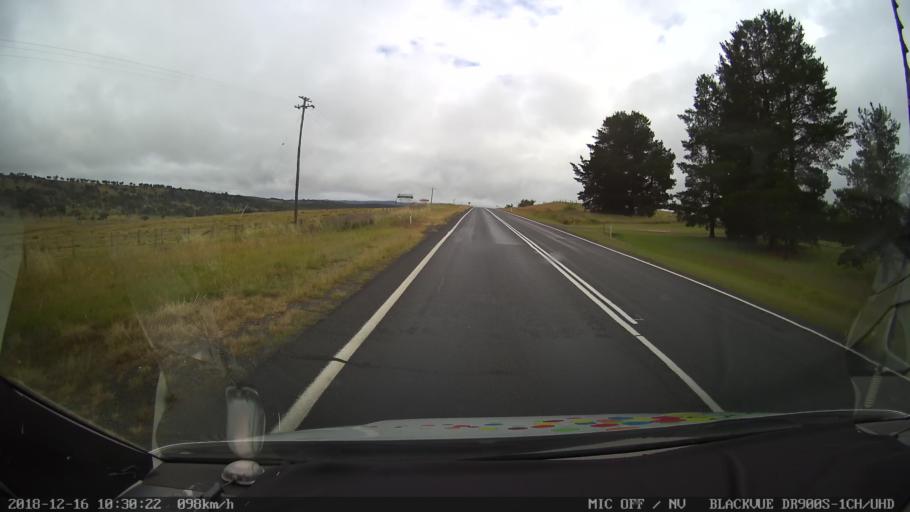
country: AU
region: New South Wales
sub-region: Tenterfield Municipality
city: Carrolls Creek
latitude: -29.0942
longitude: 152.0024
